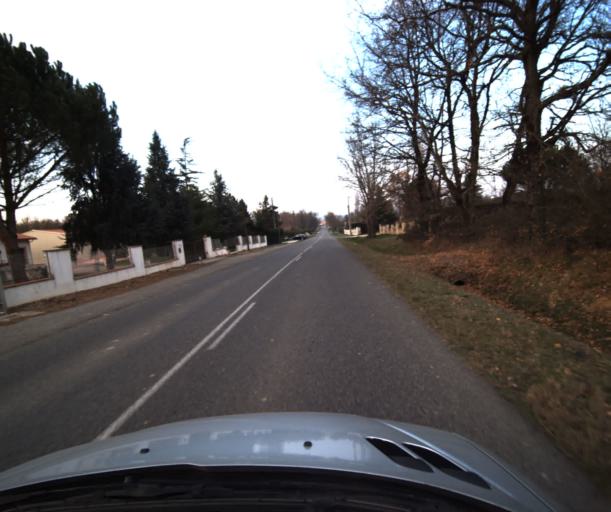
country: FR
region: Midi-Pyrenees
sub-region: Departement du Tarn-et-Garonne
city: Labastide-Saint-Pierre
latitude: 43.9044
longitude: 1.3687
